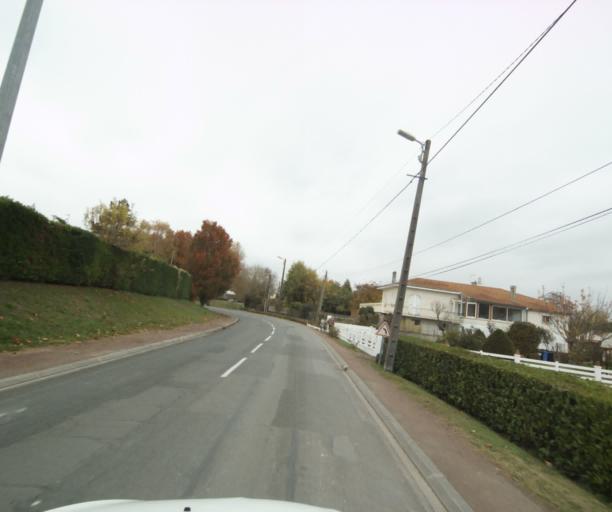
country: FR
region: Poitou-Charentes
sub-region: Departement de la Charente-Maritime
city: Saintes
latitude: 45.7397
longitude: -0.6257
